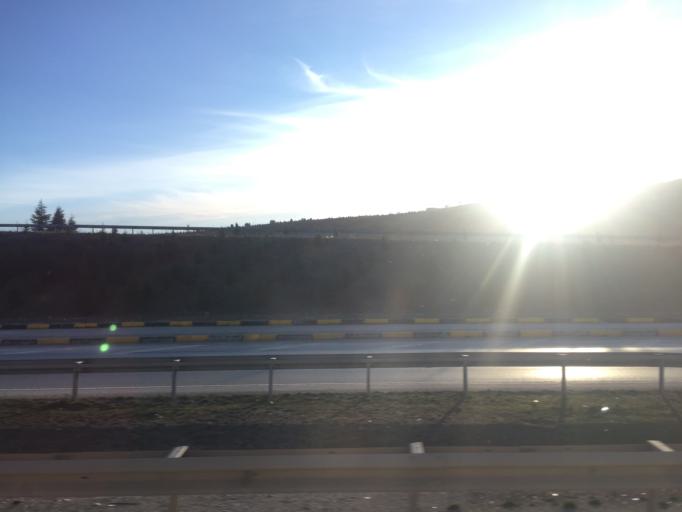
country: TR
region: Kirikkale
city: Yahsihan
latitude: 39.8738
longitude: 33.4447
